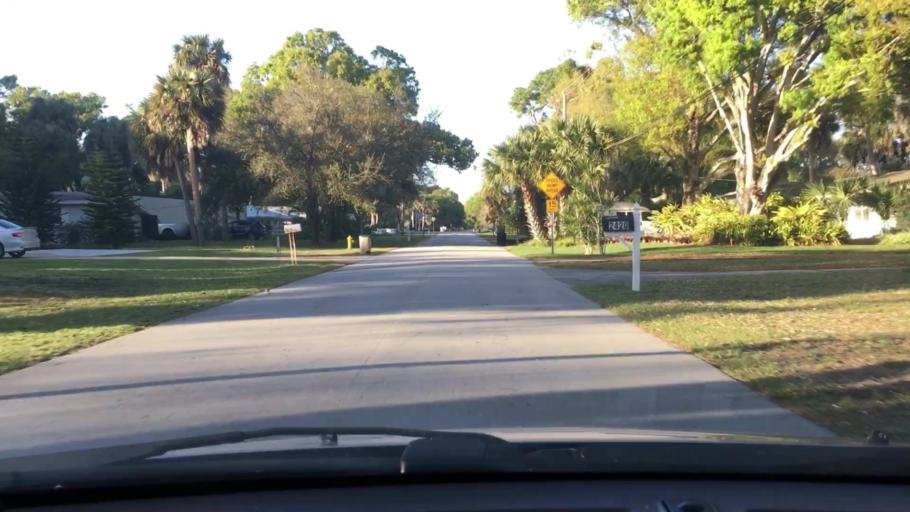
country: US
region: Florida
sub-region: Indian River County
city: Vero Beach South
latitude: 27.6446
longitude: -80.4409
